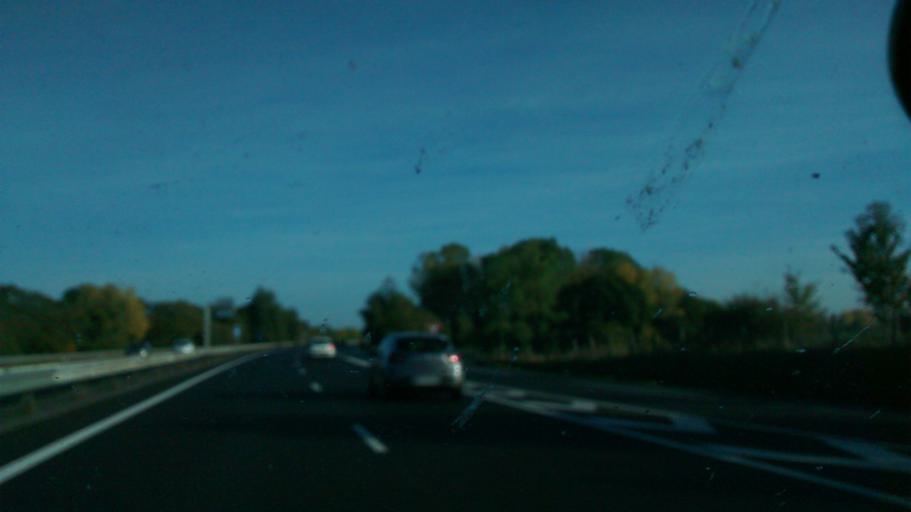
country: FR
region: Brittany
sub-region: Departement des Cotes-d'Armor
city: Plestan
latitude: 48.4182
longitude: -2.4406
